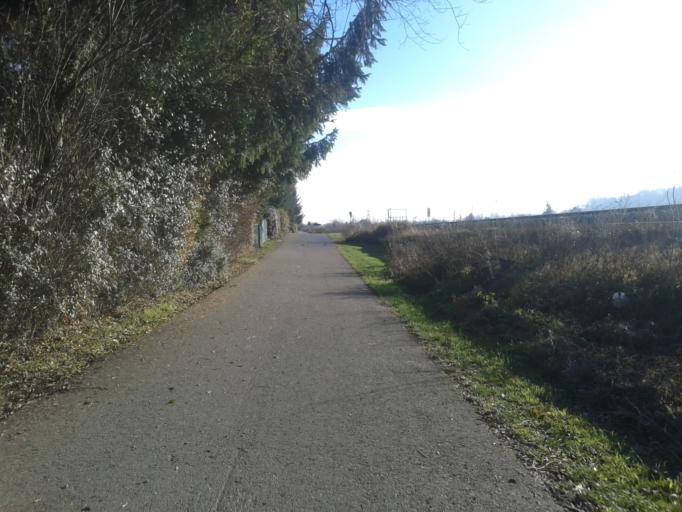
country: DE
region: Baden-Wuerttemberg
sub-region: Tuebingen Region
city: Dornstadt
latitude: 48.4100
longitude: 9.9283
